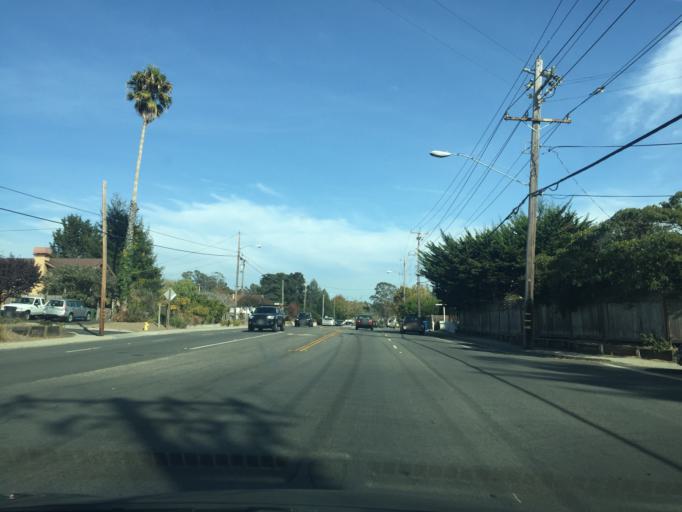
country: US
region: California
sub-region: Santa Cruz County
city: Soquel
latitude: 36.9873
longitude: -121.9493
